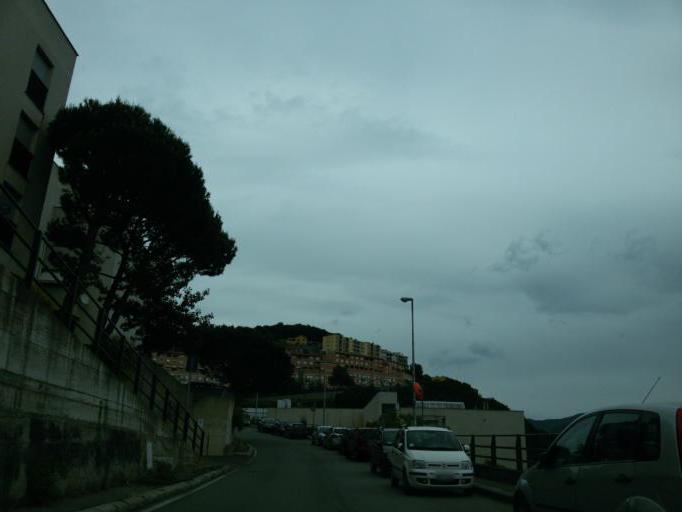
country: IT
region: Liguria
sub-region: Provincia di Genova
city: Piccarello
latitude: 44.4407
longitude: 8.9750
